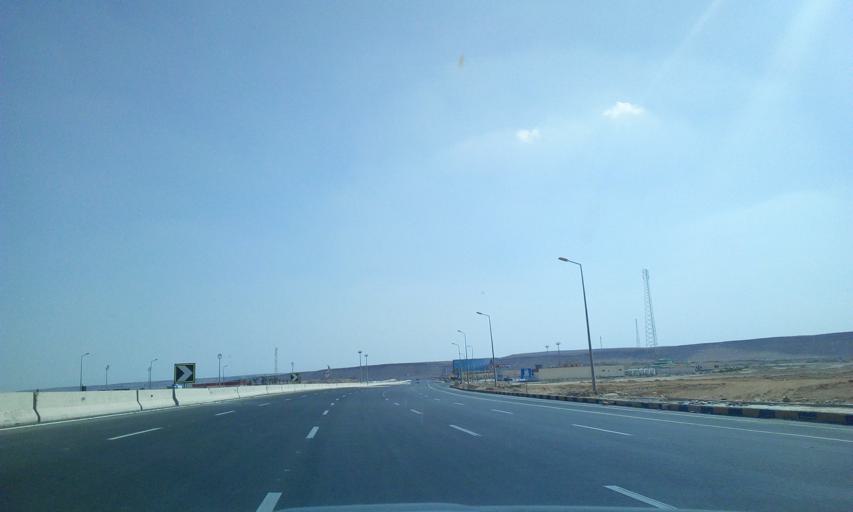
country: EG
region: As Suways
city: Ain Sukhna
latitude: 29.8091
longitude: 31.8963
